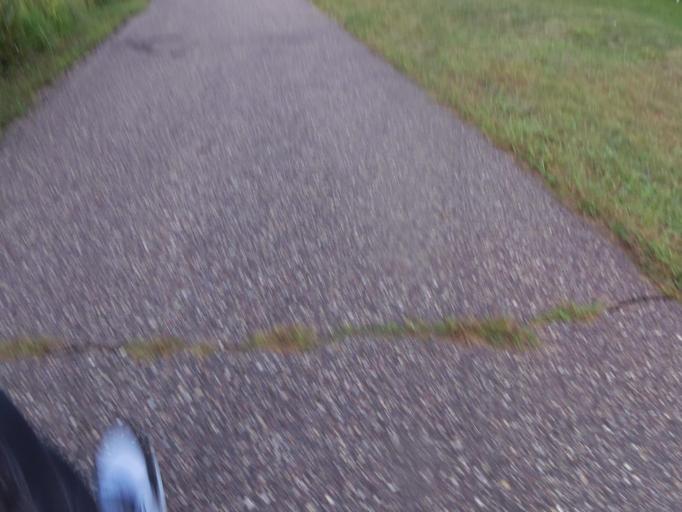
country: US
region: Minnesota
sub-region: Scott County
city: Prior Lake
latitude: 44.7017
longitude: -93.4468
